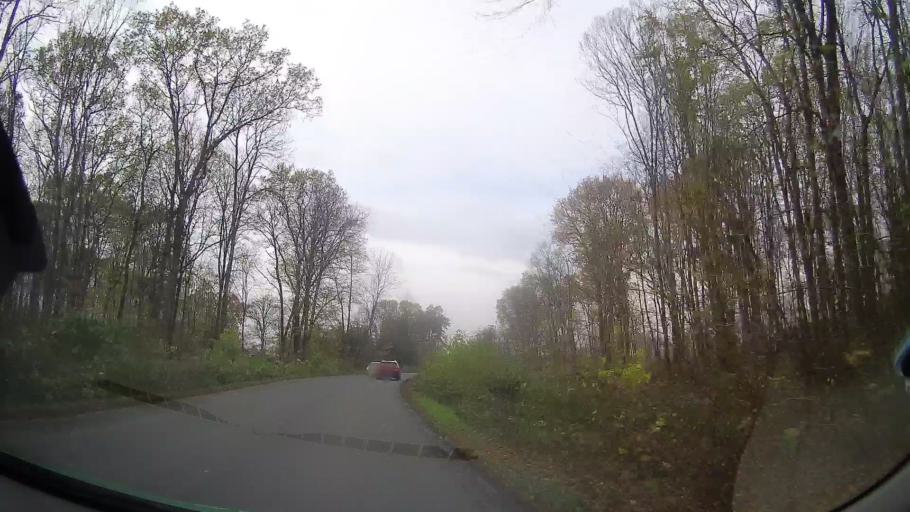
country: RO
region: Prahova
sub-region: Comuna Gorgota
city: Potigrafu
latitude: 44.7696
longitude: 26.1105
